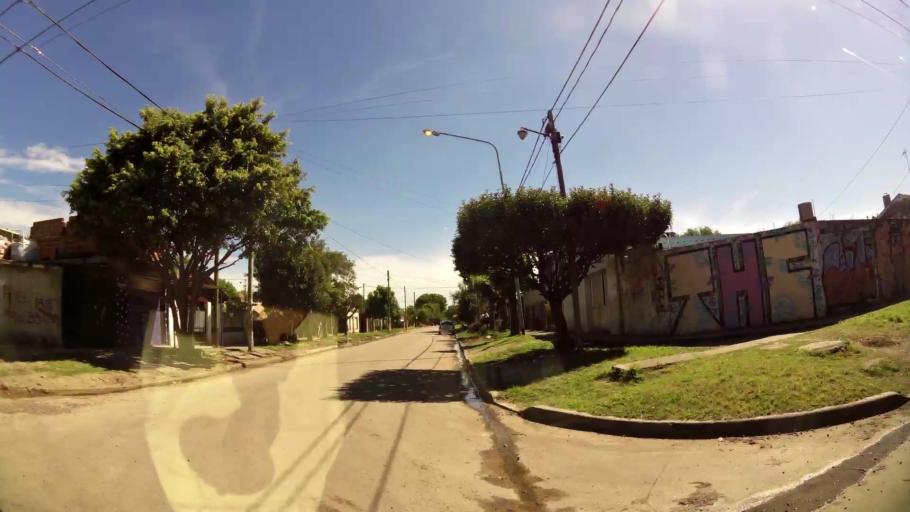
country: AR
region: Buenos Aires
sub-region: Partido de Almirante Brown
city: Adrogue
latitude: -34.7780
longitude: -58.3497
